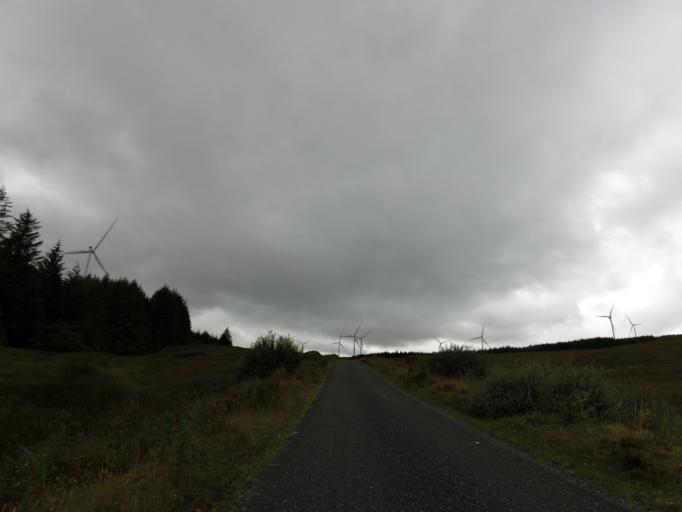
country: IE
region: Connaught
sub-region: County Galway
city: Oughterard
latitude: 53.3843
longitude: -9.3671
